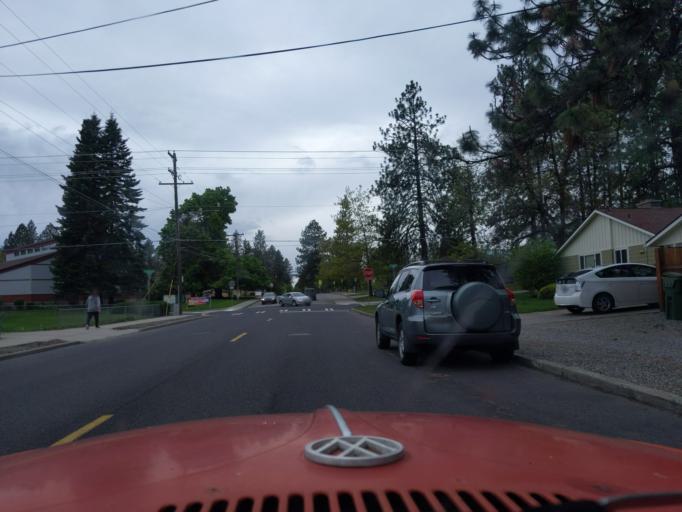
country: US
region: Washington
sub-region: Spokane County
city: Spokane
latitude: 47.6173
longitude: -117.3786
